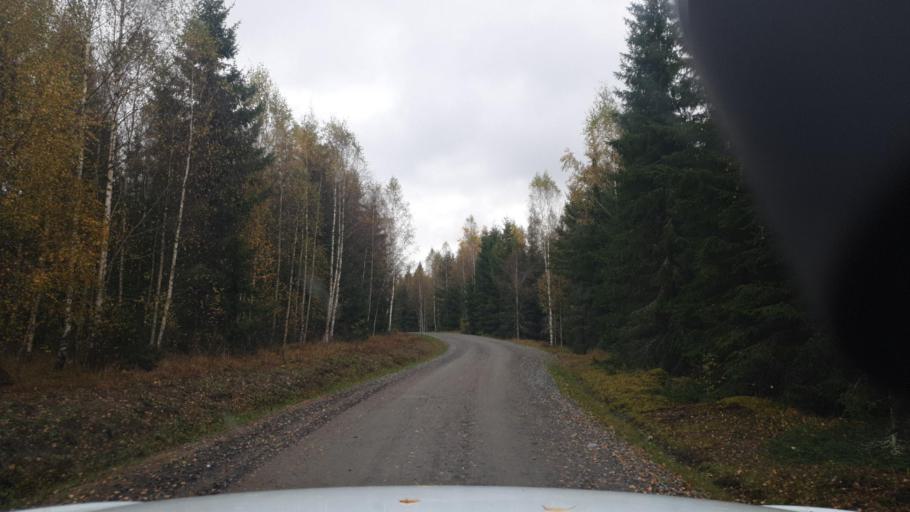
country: SE
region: Vaermland
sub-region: Karlstads Kommun
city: Edsvalla
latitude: 59.4651
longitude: 13.1217
